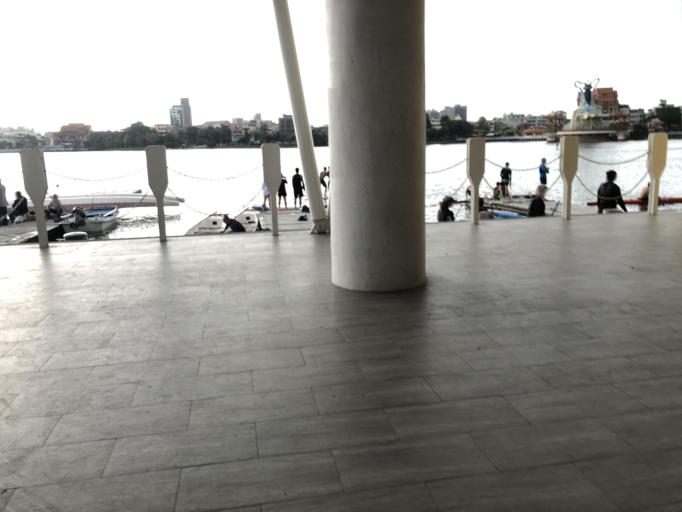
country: TW
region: Kaohsiung
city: Kaohsiung
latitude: 22.6827
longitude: 120.2982
